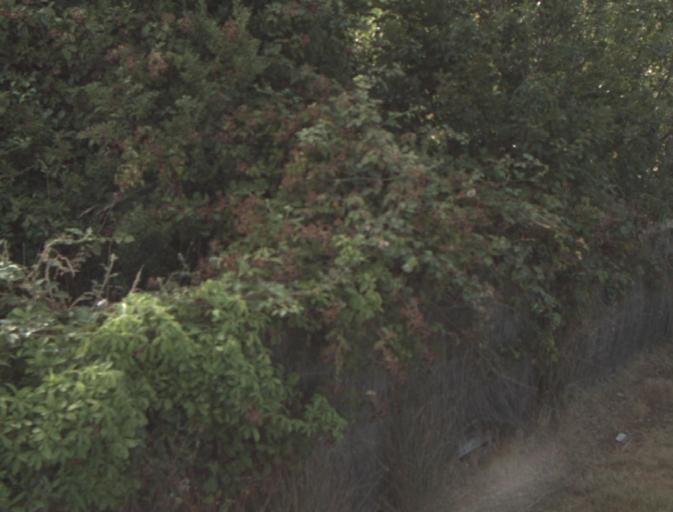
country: AU
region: Tasmania
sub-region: Launceston
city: Mayfield
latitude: -41.2939
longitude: 147.2174
